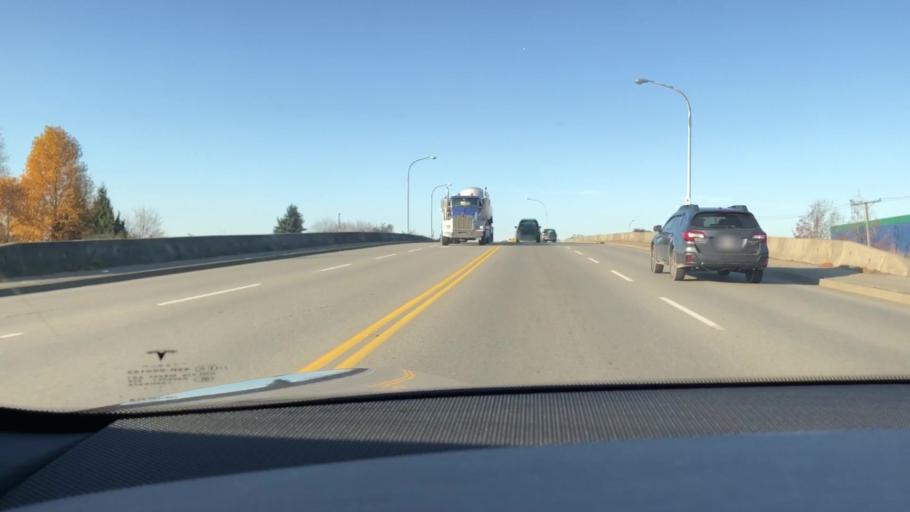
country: CA
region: British Columbia
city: Richmond
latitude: 49.1846
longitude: -123.0751
